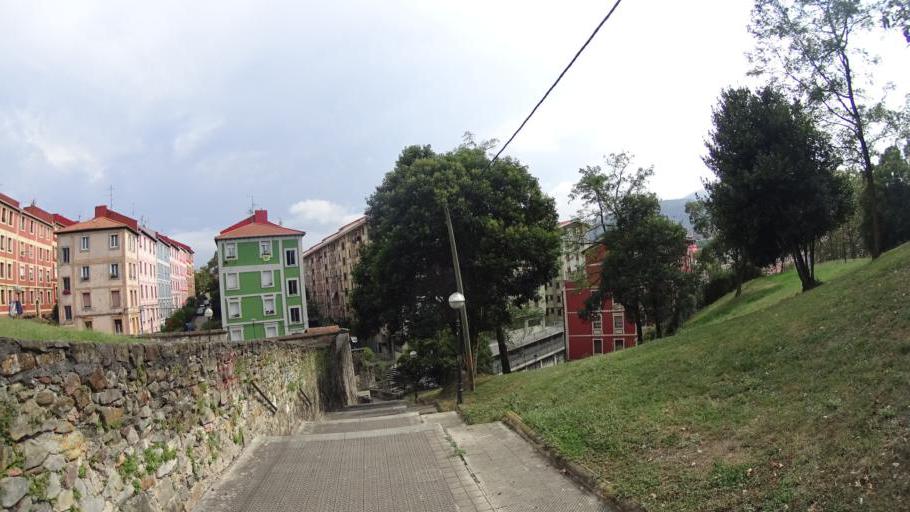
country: ES
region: Basque Country
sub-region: Bizkaia
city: Bilbao
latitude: 43.2600
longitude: -2.9206
